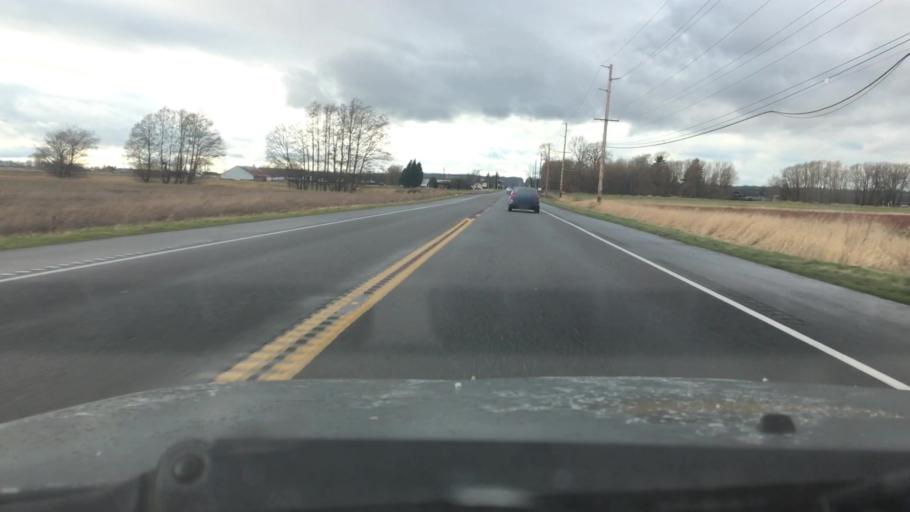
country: US
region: Washington
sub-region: Whatcom County
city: Ferndale
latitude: 48.8191
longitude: -122.5986
